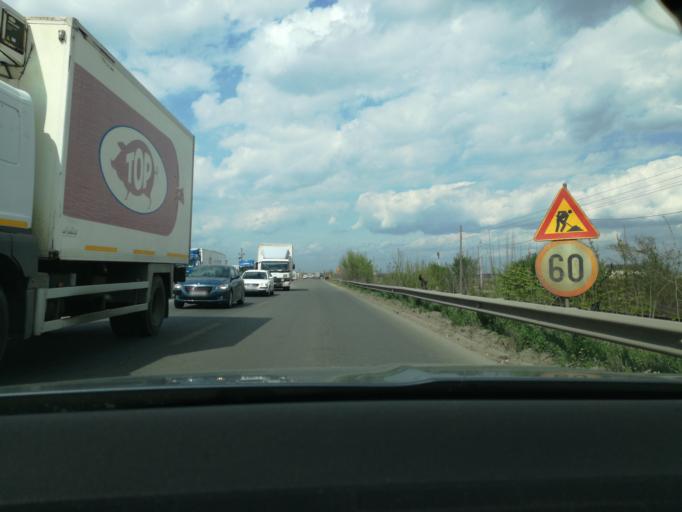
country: RO
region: Ilfov
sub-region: Comuna Chiajna
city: Chiajna
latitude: 44.4414
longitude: 25.9665
